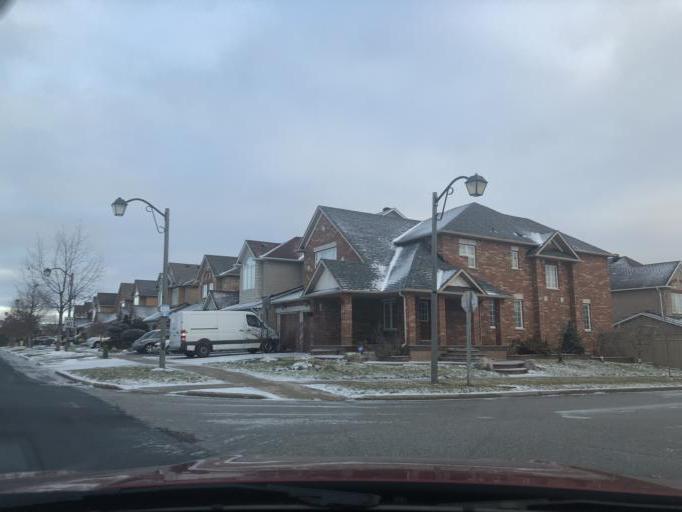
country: CA
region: Ontario
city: Markham
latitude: 43.8659
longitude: -79.2403
